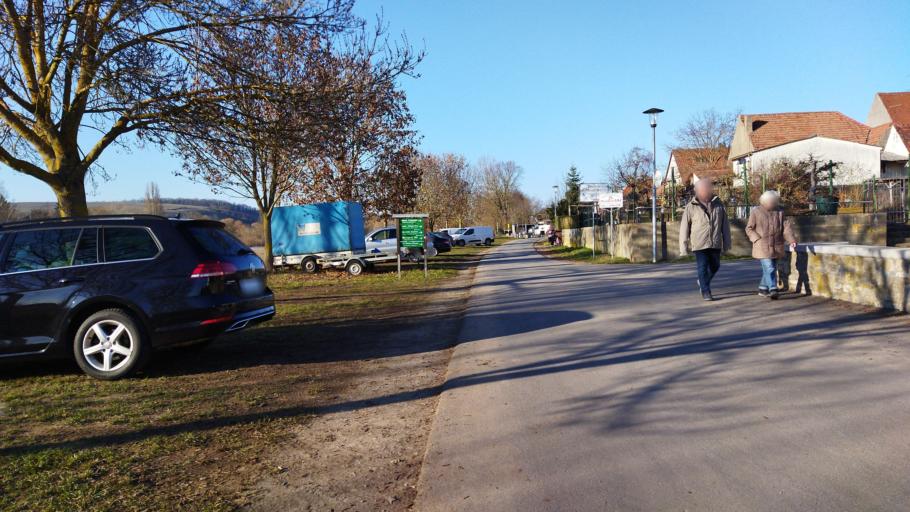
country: DE
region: Bavaria
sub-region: Regierungsbezirk Unterfranken
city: Albertshofen
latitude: 49.7713
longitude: 10.1576
